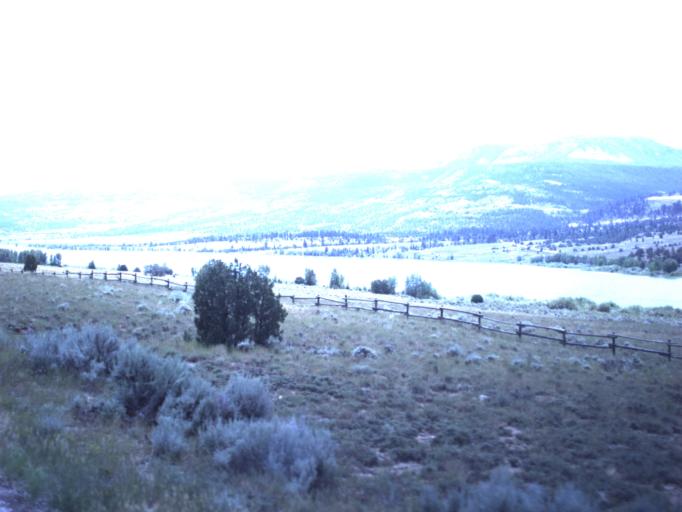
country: US
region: Utah
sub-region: Emery County
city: Orangeville
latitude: 39.3166
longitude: -111.2763
